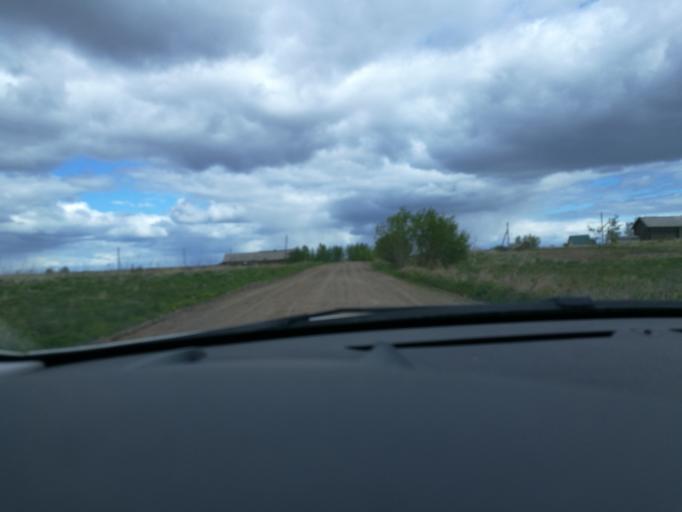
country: RU
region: Arkhangelskaya
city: Lukovetskiy
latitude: 64.2567
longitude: 41.7998
